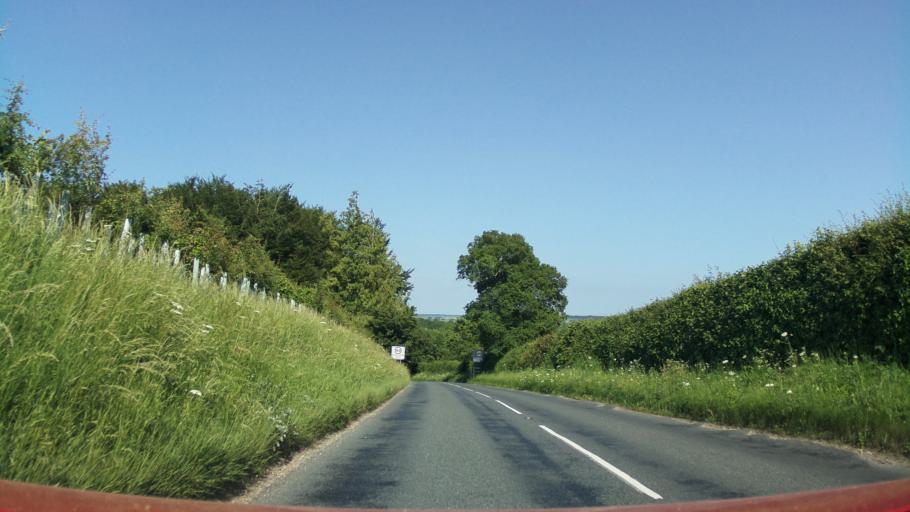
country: GB
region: England
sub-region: Hampshire
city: Andover
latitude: 51.2151
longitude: -1.3819
